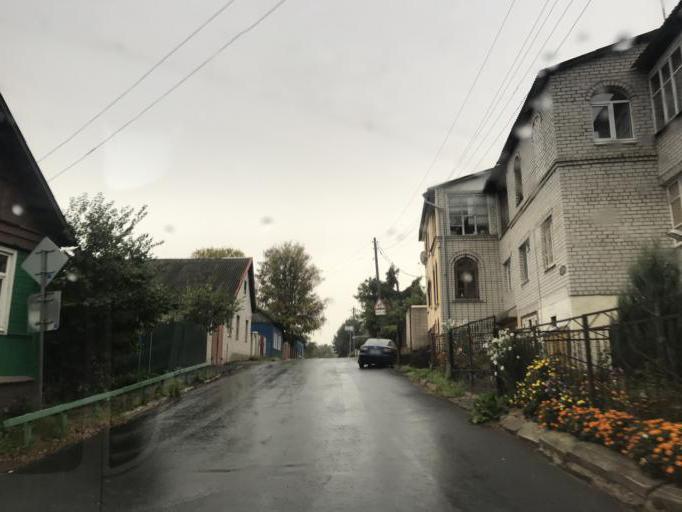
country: BY
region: Mogilev
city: Mahilyow
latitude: 53.8979
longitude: 30.3236
